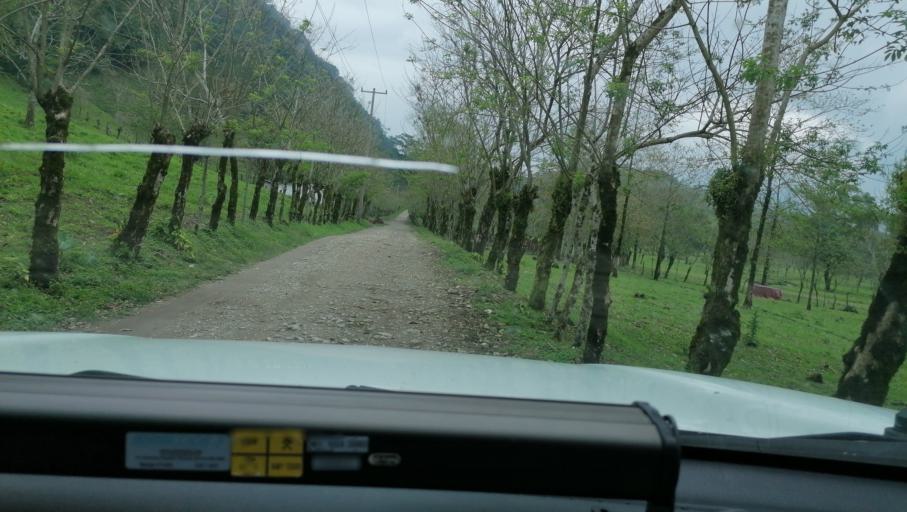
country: MX
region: Chiapas
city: Ixtacomitan
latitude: 17.3510
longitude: -93.1566
